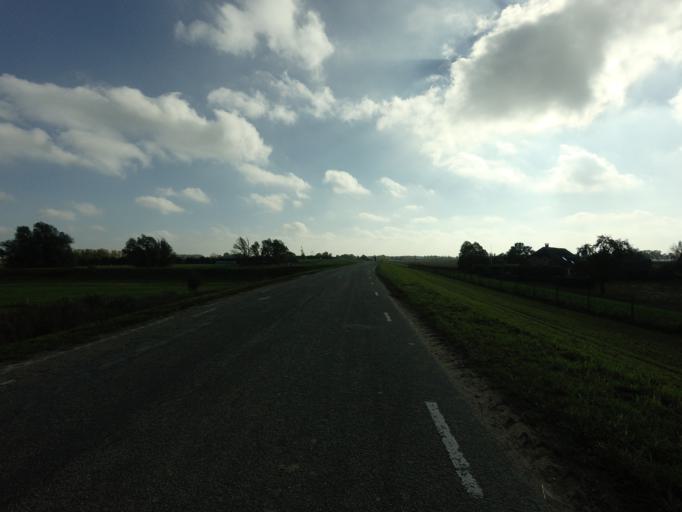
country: NL
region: Gelderland
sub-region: Gemeente Culemborg
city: Culemborg
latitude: 51.9601
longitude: 5.2682
